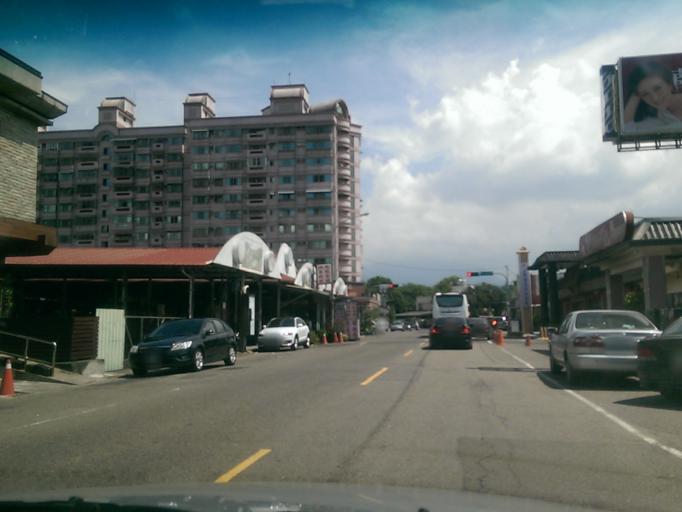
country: TW
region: Taiwan
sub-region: Nantou
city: Puli
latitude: 23.9723
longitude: 120.9674
